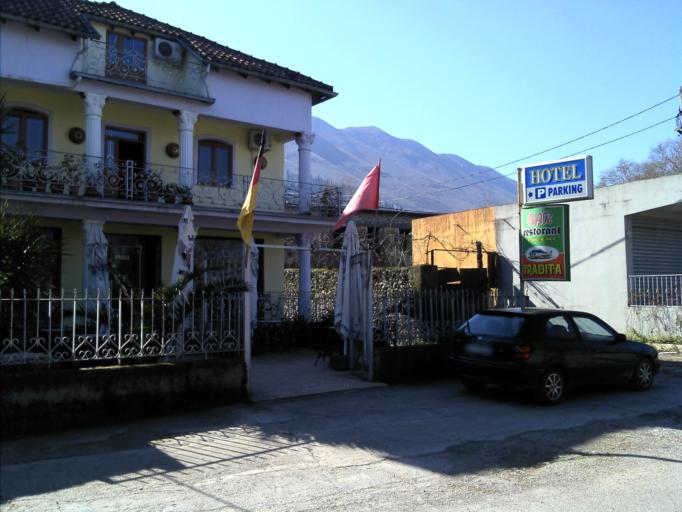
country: AL
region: Shkoder
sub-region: Rrethi i Shkodres
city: Berdica e Madhe
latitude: 42.0592
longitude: 19.4569
